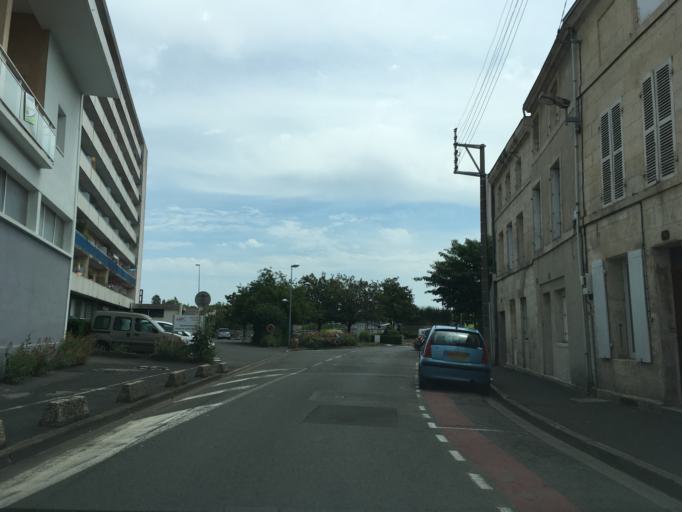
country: FR
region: Poitou-Charentes
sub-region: Departement des Deux-Sevres
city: Niort
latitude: 46.3190
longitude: -0.4571
